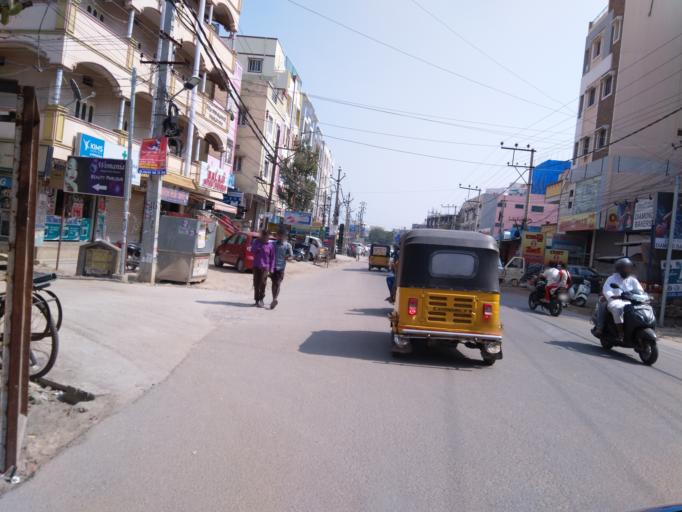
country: IN
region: Telangana
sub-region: Rangareddi
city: Kukatpalli
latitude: 17.4984
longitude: 78.4110
